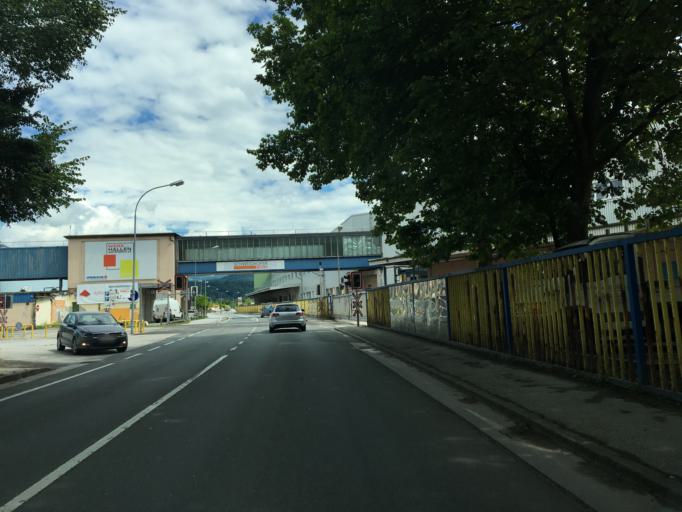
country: AT
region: Salzburg
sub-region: Politischer Bezirk Hallein
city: Hallein
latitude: 47.6749
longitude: 13.1114
